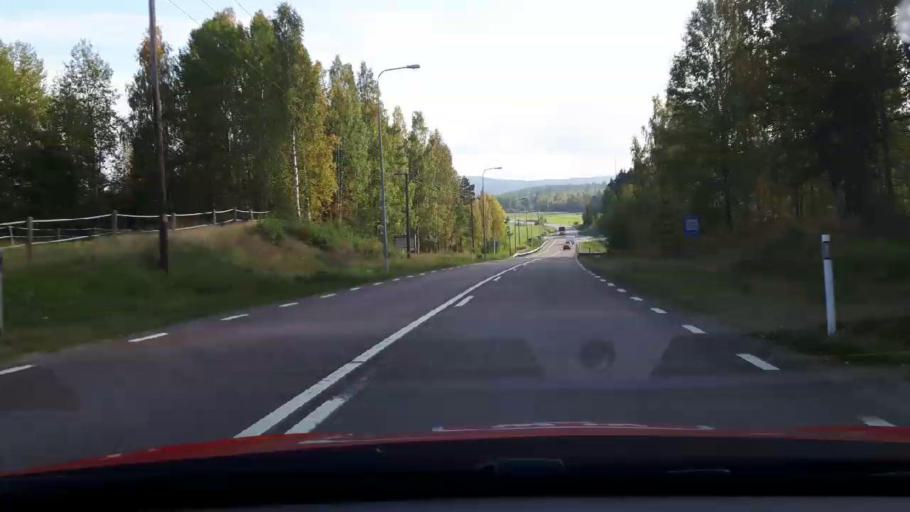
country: SE
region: Gaevleborg
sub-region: Bollnas Kommun
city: Kilafors
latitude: 61.2138
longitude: 16.6038
